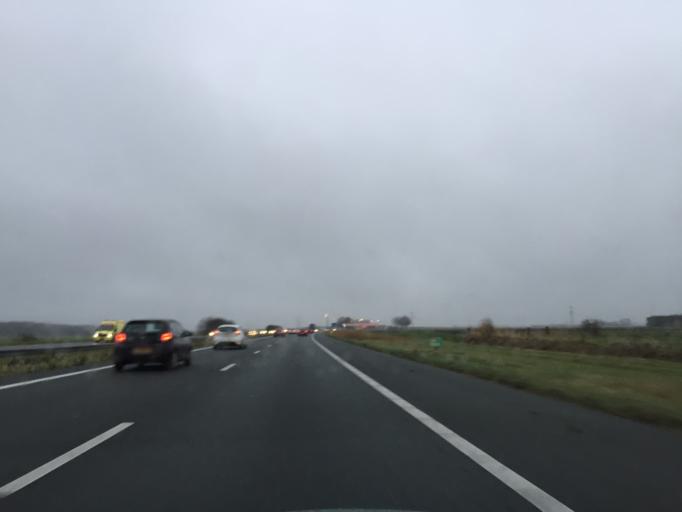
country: NL
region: Zeeland
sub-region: Gemeente Goes
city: Goes
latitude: 51.4855
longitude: 3.8408
